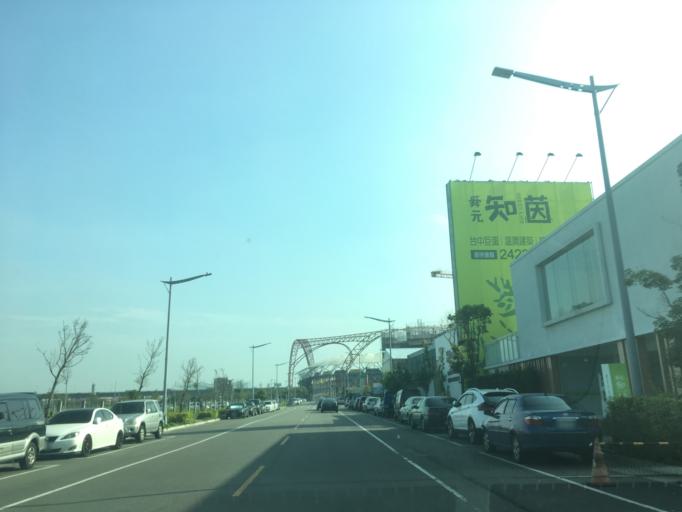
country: TW
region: Taiwan
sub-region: Taichung City
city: Taichung
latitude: 24.1957
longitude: 120.6826
